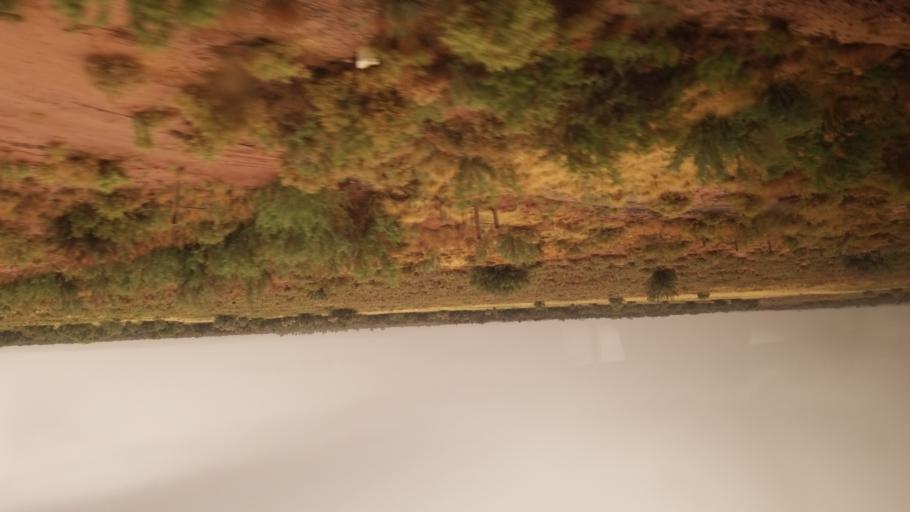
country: US
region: Arizona
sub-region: Navajo County
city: Joseph City
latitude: 34.9675
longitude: -110.4797
